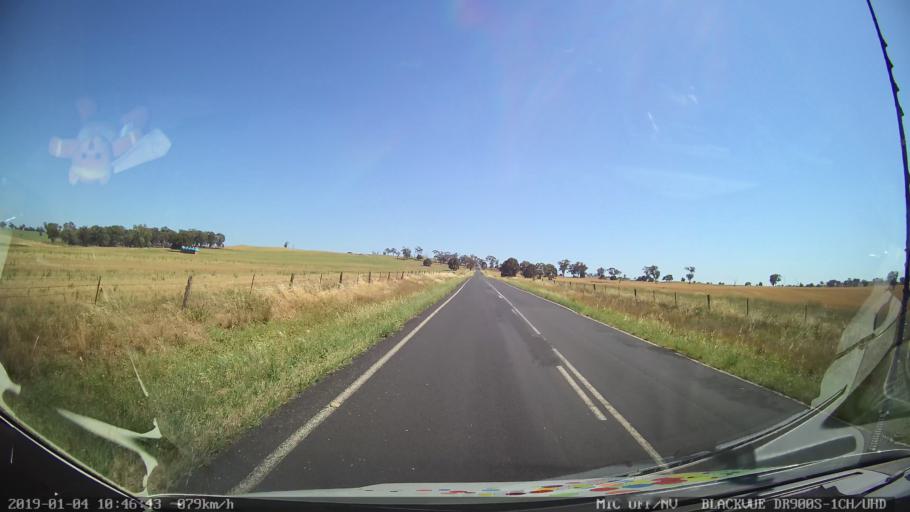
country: AU
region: New South Wales
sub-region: Cabonne
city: Molong
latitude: -33.2780
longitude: 148.7214
